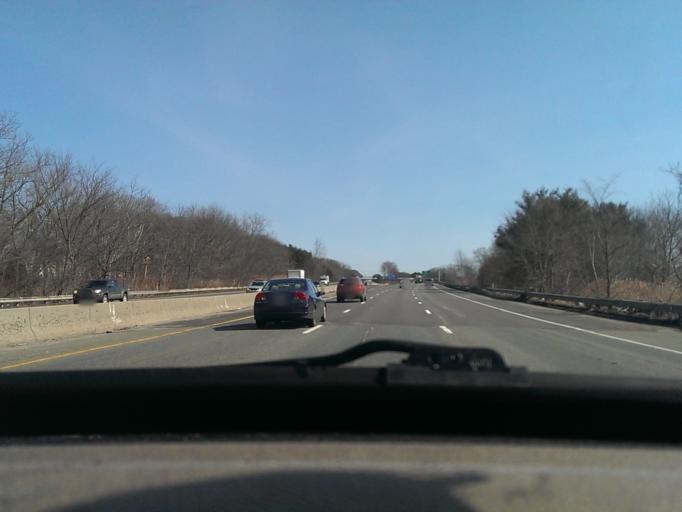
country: US
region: Massachusetts
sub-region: Bristol County
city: Seekonk
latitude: 41.8065
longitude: -71.3391
